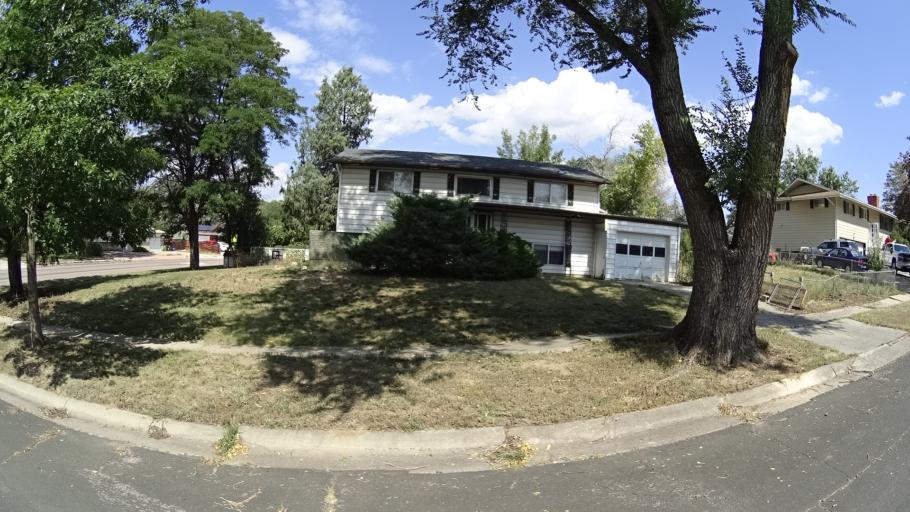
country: US
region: Colorado
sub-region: El Paso County
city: Colorado Springs
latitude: 38.8281
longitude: -104.7784
